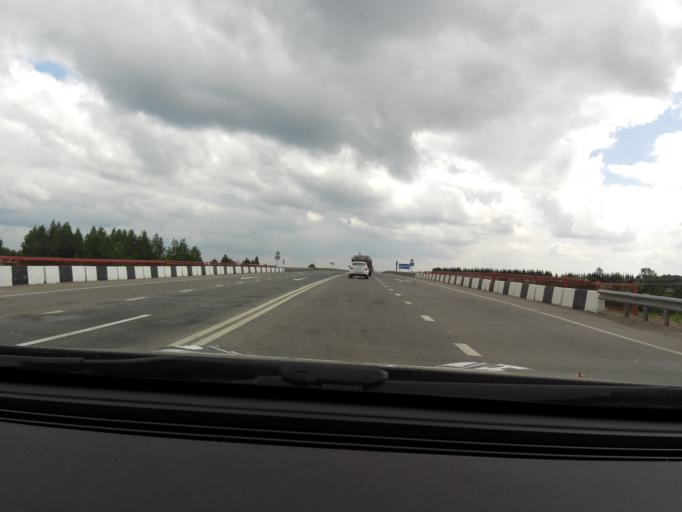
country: RU
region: Perm
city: Kungur
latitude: 57.4039
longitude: 56.8890
